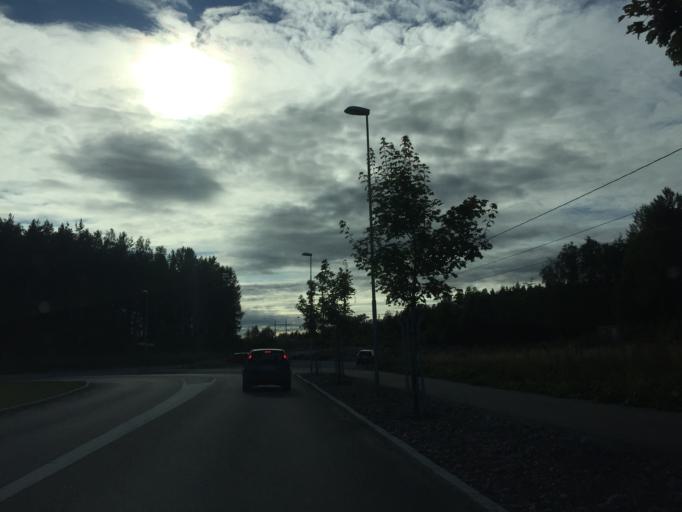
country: SE
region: Vaestmanland
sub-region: Vasteras
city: Vasteras
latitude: 59.6095
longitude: 16.4478
